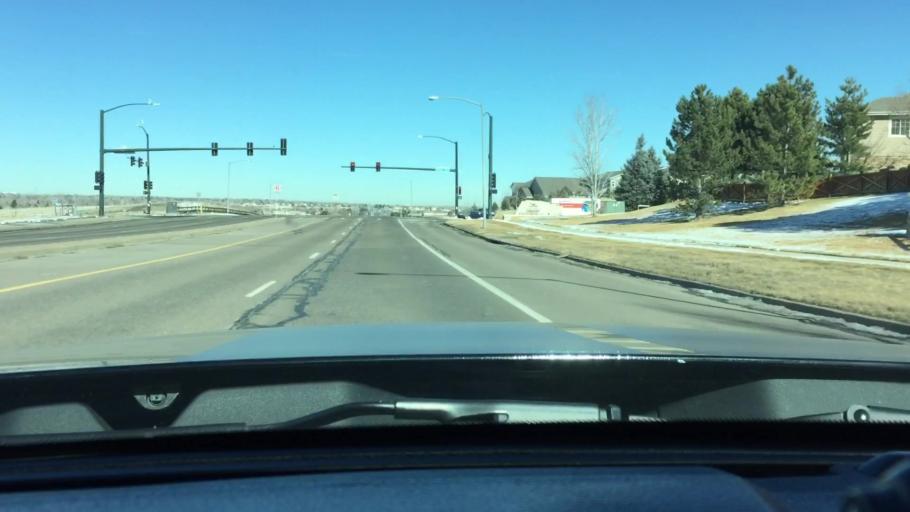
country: US
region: Colorado
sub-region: Broomfield County
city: Broomfield
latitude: 39.8917
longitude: -105.0529
